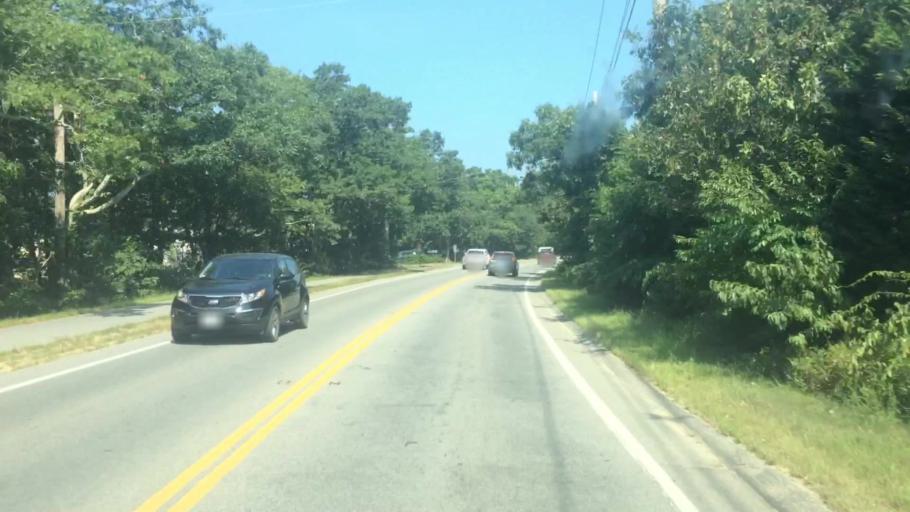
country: US
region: Massachusetts
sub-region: Dukes County
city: Vineyard Haven
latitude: 41.4253
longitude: -70.6075
